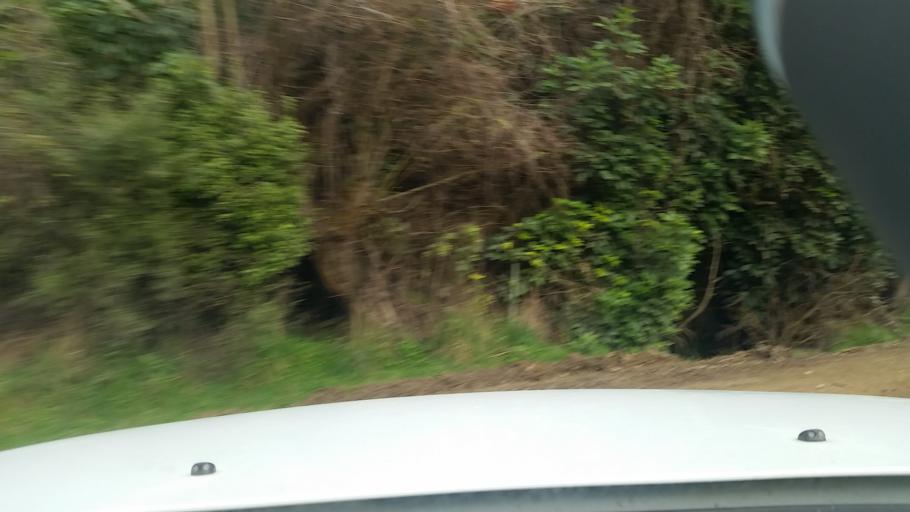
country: NZ
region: Canterbury
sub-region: Christchurch City
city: Christchurch
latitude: -43.6352
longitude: 172.7350
